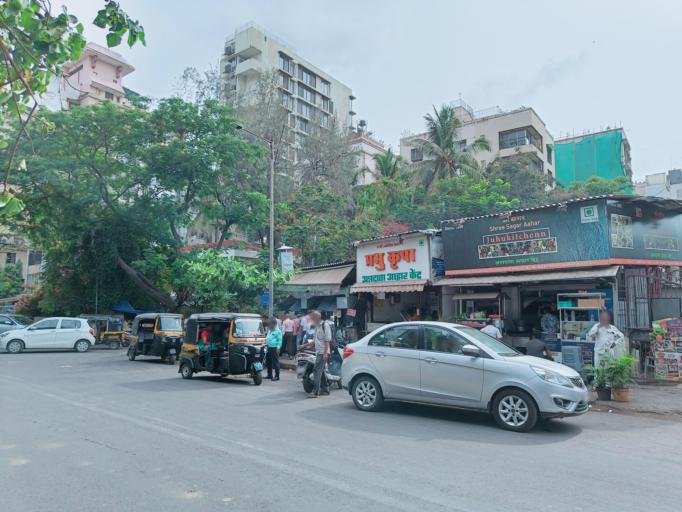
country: IN
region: Maharashtra
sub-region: Mumbai Suburban
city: Mumbai
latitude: 19.1102
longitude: 72.8338
